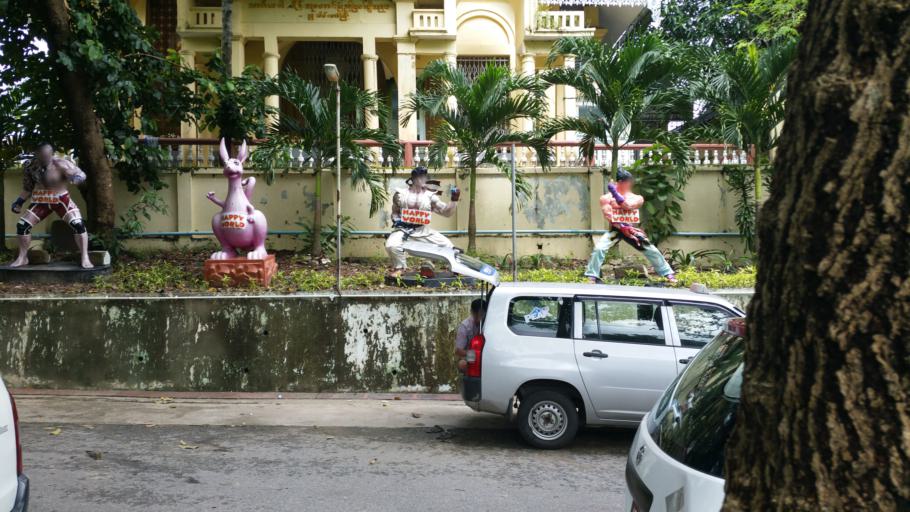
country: MM
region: Yangon
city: Yangon
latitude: 16.7946
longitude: 96.1500
